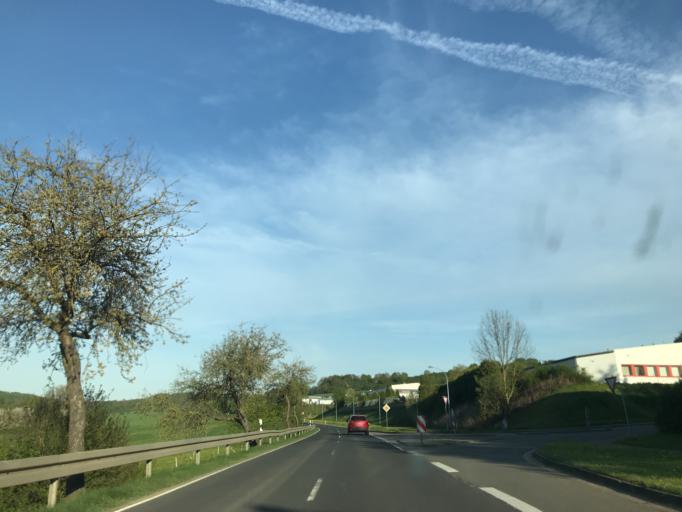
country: DE
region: Thuringia
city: Geisleden
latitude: 51.3452
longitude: 10.2048
